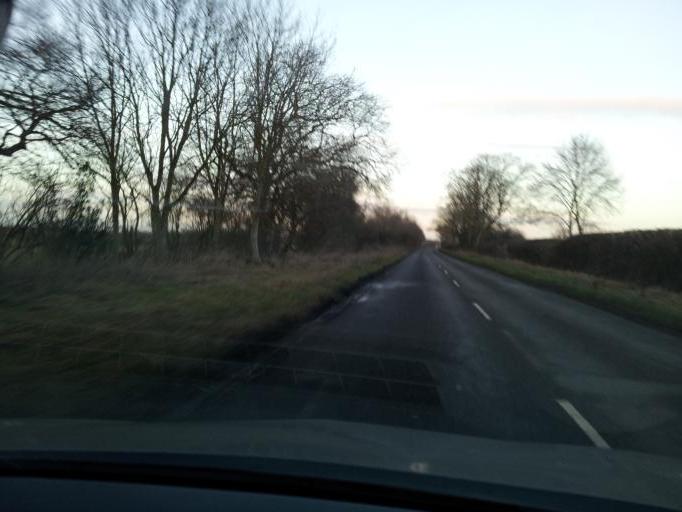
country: GB
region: England
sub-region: Leicestershire
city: Houghton on the Hill
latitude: 52.6087
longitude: -1.0176
